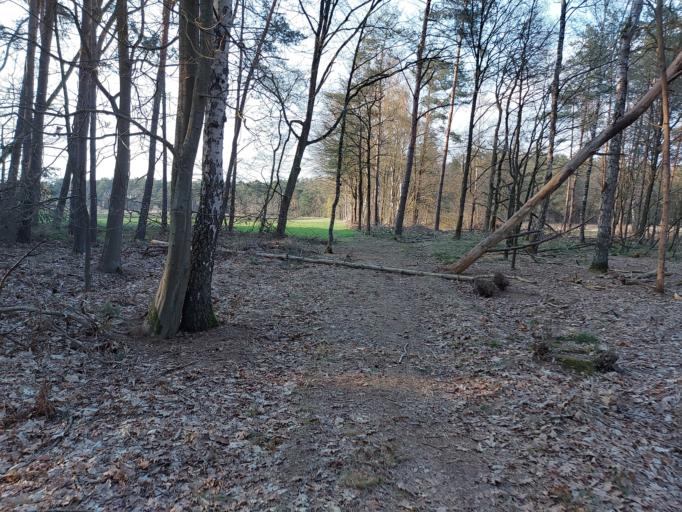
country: BE
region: Flanders
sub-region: Provincie Antwerpen
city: Kasterlee
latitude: 51.2215
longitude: 4.9872
